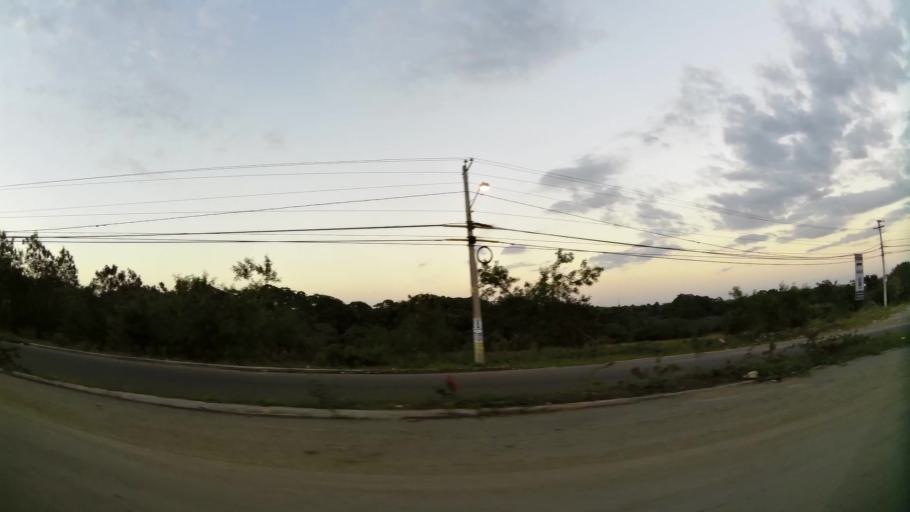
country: DO
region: Nacional
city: La Agustina
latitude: 18.5617
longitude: -69.9371
